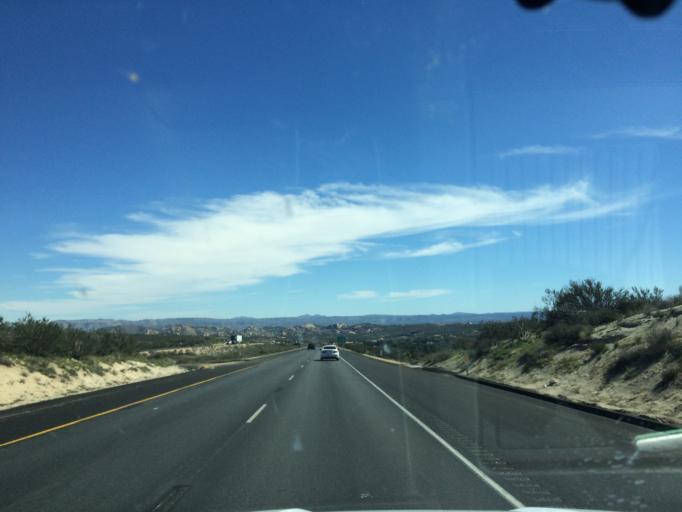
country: US
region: California
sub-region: San Diego County
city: Campo
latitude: 32.6862
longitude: -116.3037
